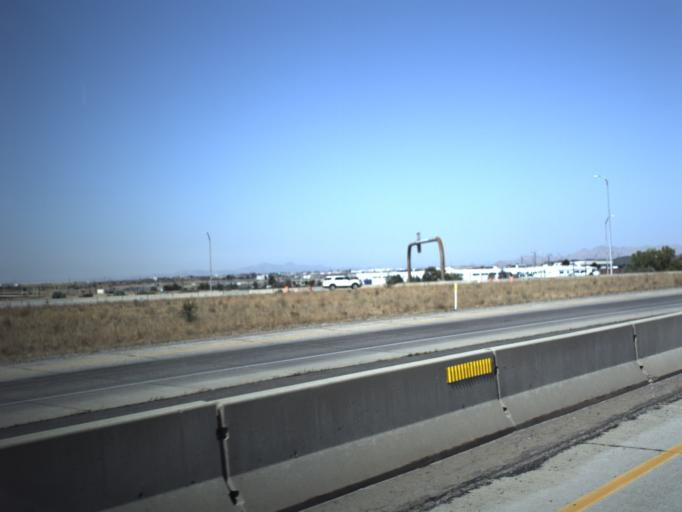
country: US
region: Utah
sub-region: Salt Lake County
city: Salt Lake City
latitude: 40.7681
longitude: -111.9481
